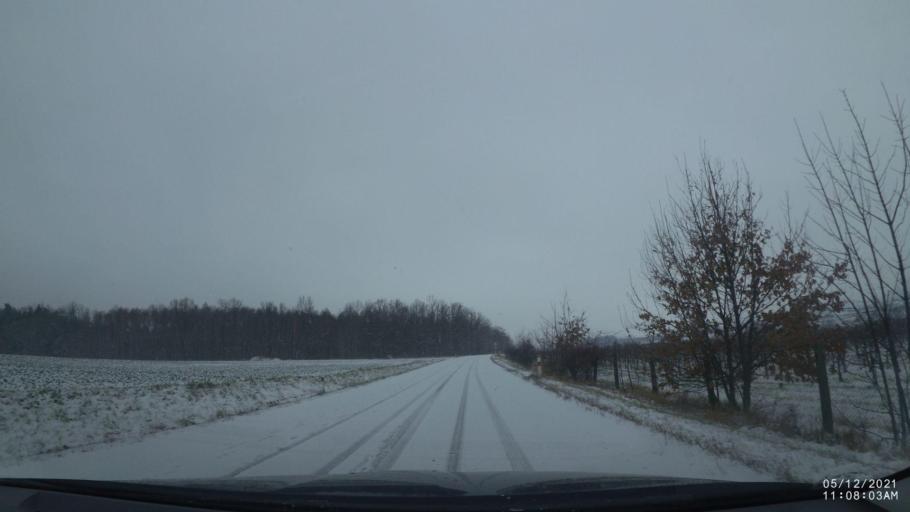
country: CZ
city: Solnice
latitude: 50.1744
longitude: 16.2232
